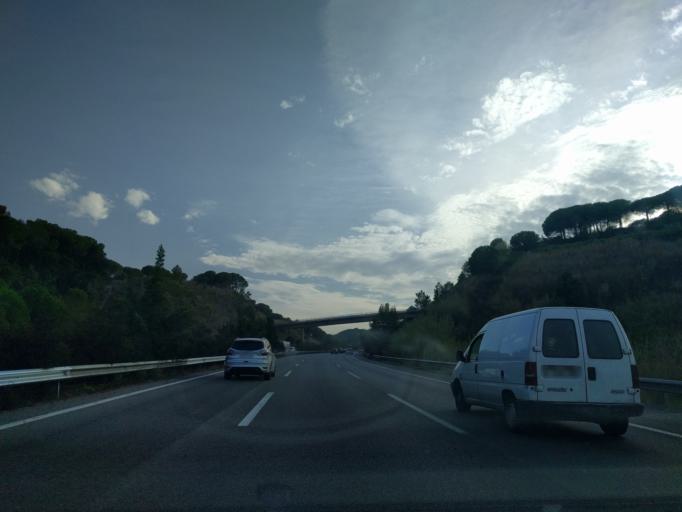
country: ES
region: Catalonia
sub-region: Provincia de Barcelona
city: Sant Pol de Mar
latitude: 41.6035
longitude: 2.6039
